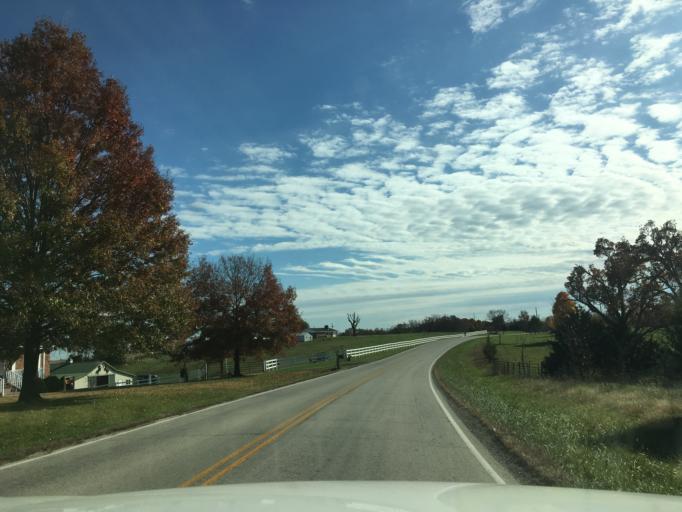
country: US
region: Missouri
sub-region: Osage County
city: Linn
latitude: 38.4342
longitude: -91.8282
